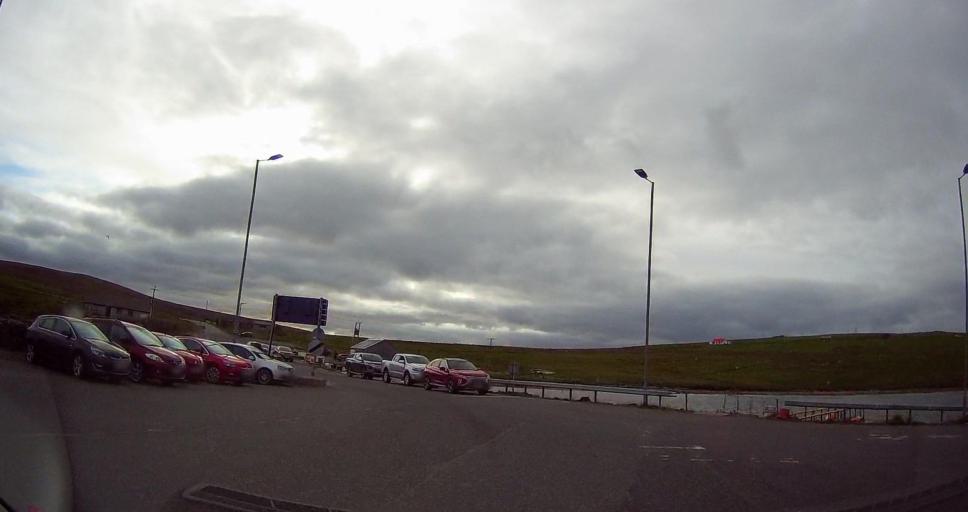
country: GB
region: Scotland
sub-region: Shetland Islands
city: Lerwick
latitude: 60.4665
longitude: -1.2070
